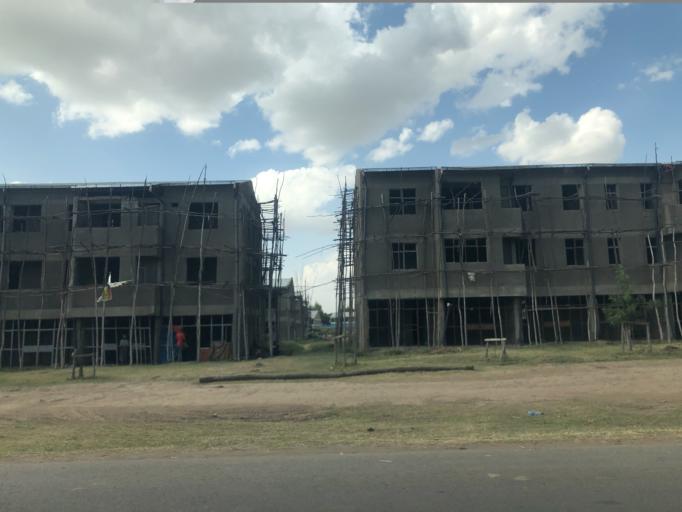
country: ET
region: Southern Nations, Nationalities, and People's Region
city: K'olito
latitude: 7.3032
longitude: 38.0875
